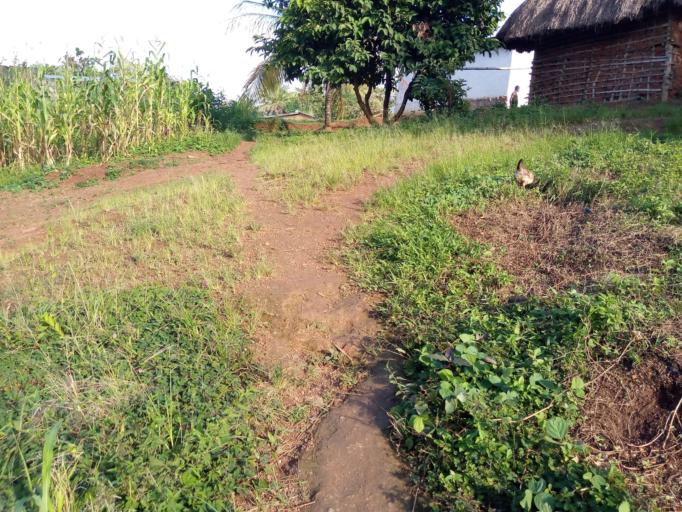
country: SL
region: Eastern Province
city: Buedu
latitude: 8.4776
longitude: -10.3377
